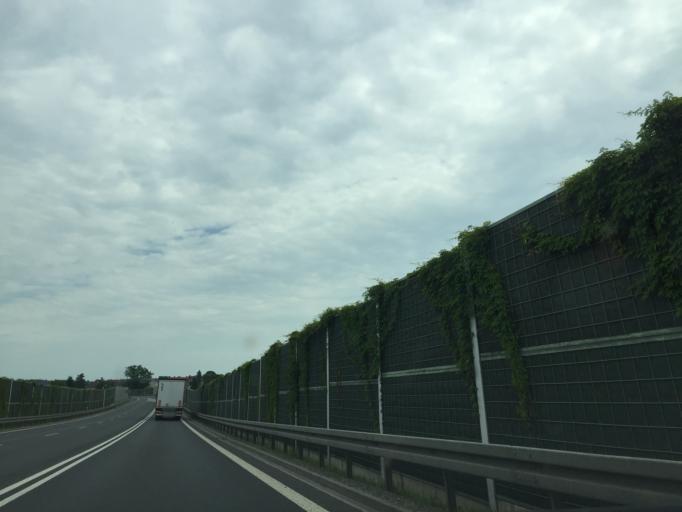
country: PL
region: Warmian-Masurian Voivodeship
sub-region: Powiat mragowski
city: Mragowo
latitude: 53.8772
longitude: 21.2917
